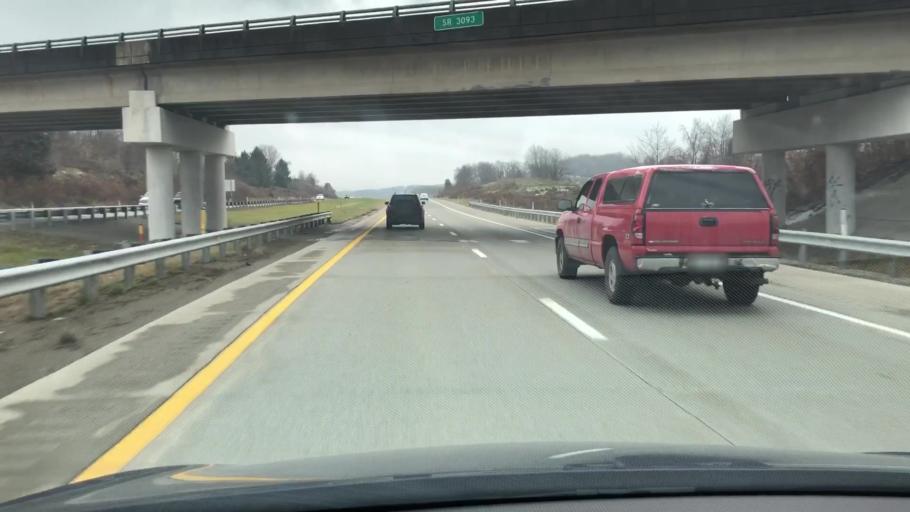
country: US
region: Pennsylvania
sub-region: Westmoreland County
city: Mount Pleasant
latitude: 40.1709
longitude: -79.5601
